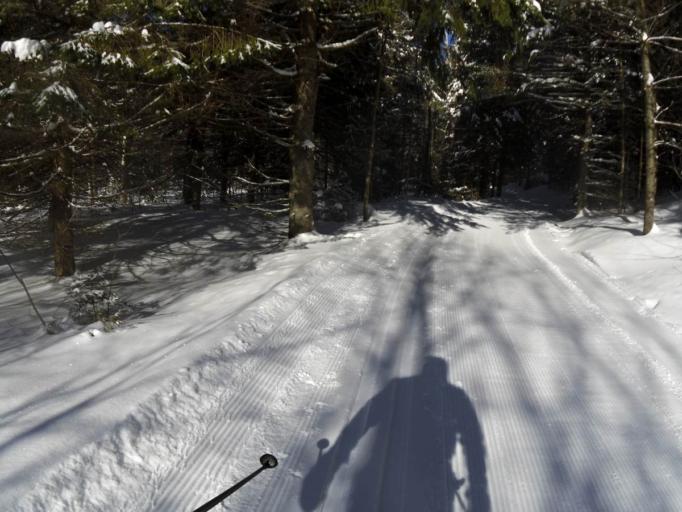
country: CA
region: Quebec
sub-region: Outaouais
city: Wakefield
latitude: 45.6209
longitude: -75.9458
